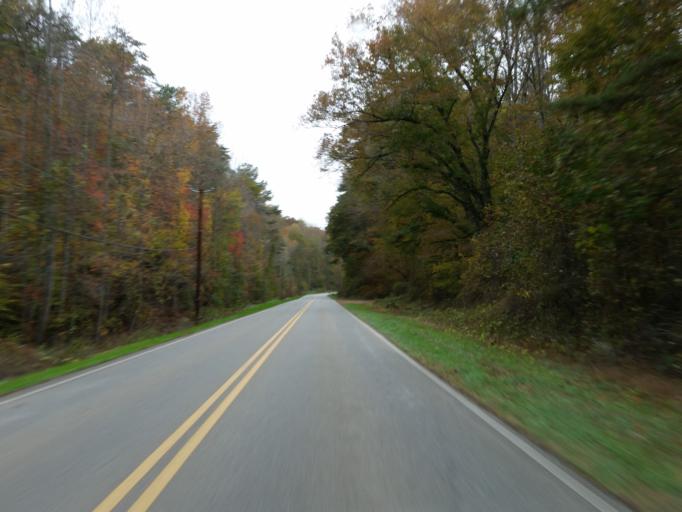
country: US
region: Georgia
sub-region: Pickens County
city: Jasper
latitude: 34.4898
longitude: -84.4237
